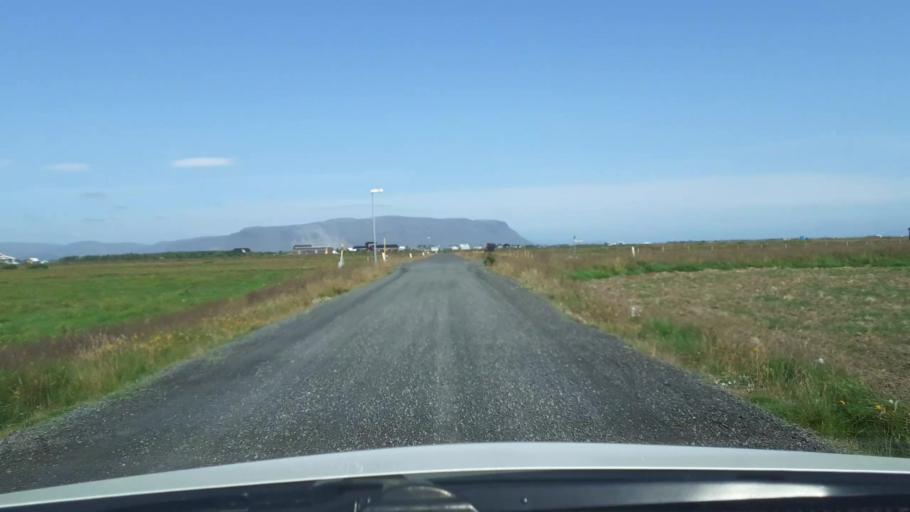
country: IS
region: South
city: Selfoss
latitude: 63.8870
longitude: -21.0912
